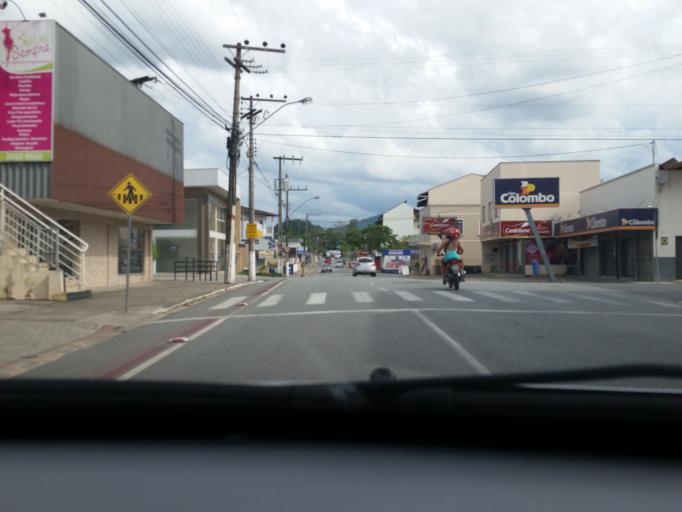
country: BR
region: Santa Catarina
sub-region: Indaial
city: Indaial
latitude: -26.8895
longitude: -49.2443
